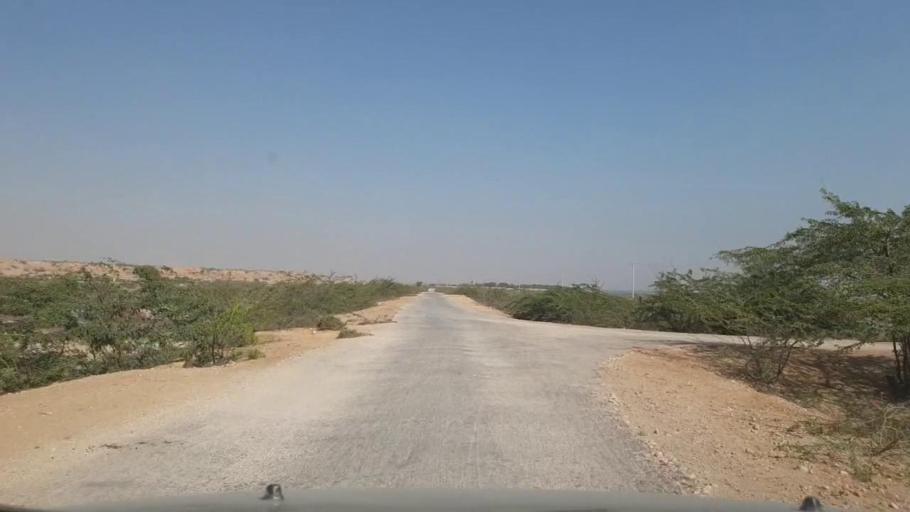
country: PK
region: Sindh
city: Thatta
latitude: 24.9846
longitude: 67.9964
